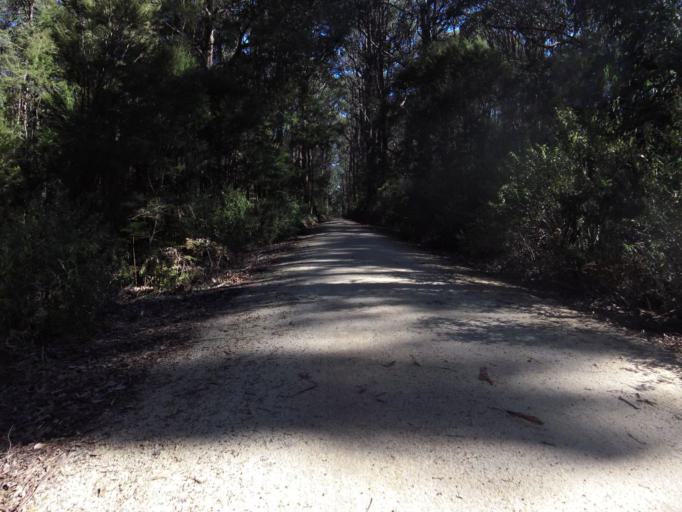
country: AU
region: Victoria
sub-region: Latrobe
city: Moe
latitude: -38.3925
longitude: 146.1798
